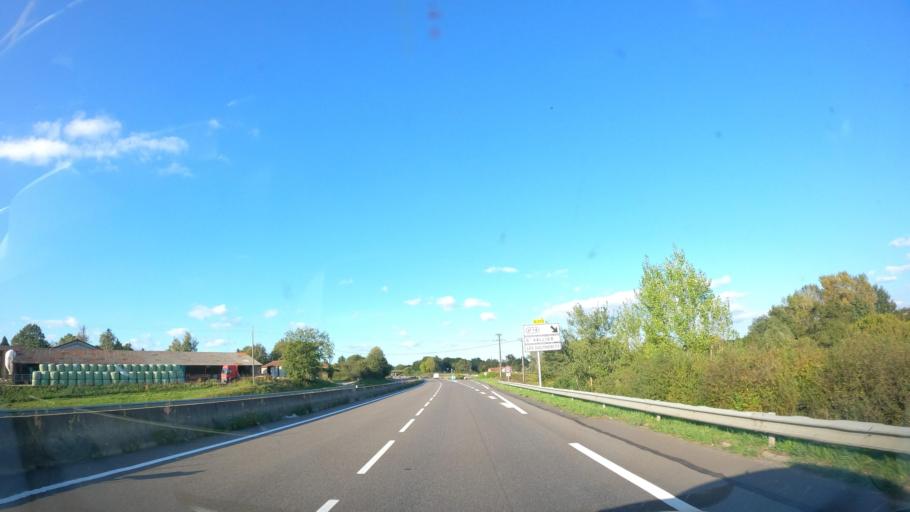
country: FR
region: Bourgogne
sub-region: Departement de Saone-et-Loire
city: Saint-Vallier
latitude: 46.6398
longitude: 4.3281
